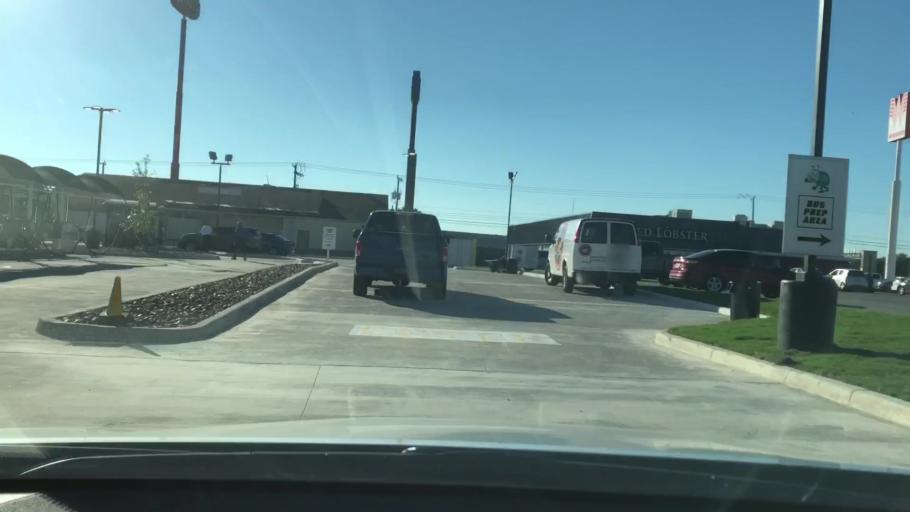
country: US
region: Texas
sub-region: Bexar County
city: Windcrest
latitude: 29.5126
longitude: -98.3952
